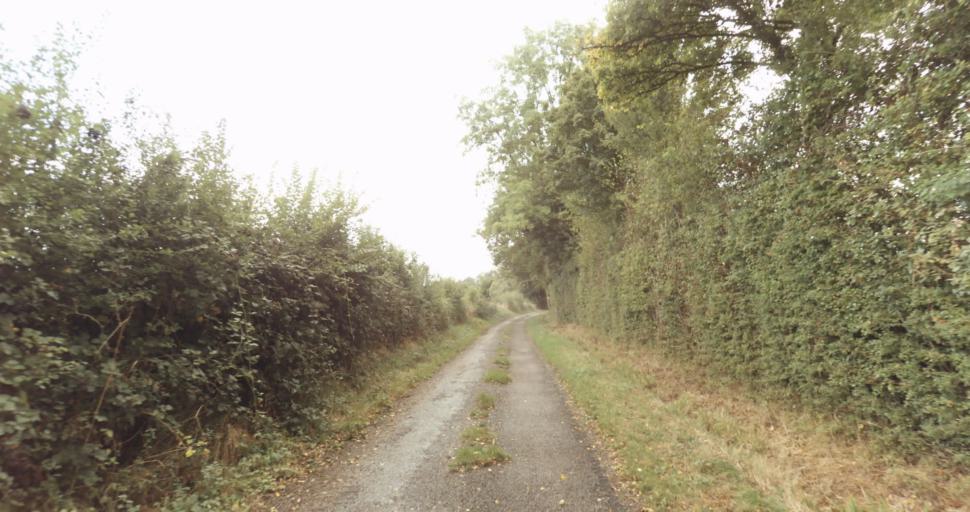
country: FR
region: Lower Normandy
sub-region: Departement de l'Orne
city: Vimoutiers
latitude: 48.8876
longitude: 0.1764
